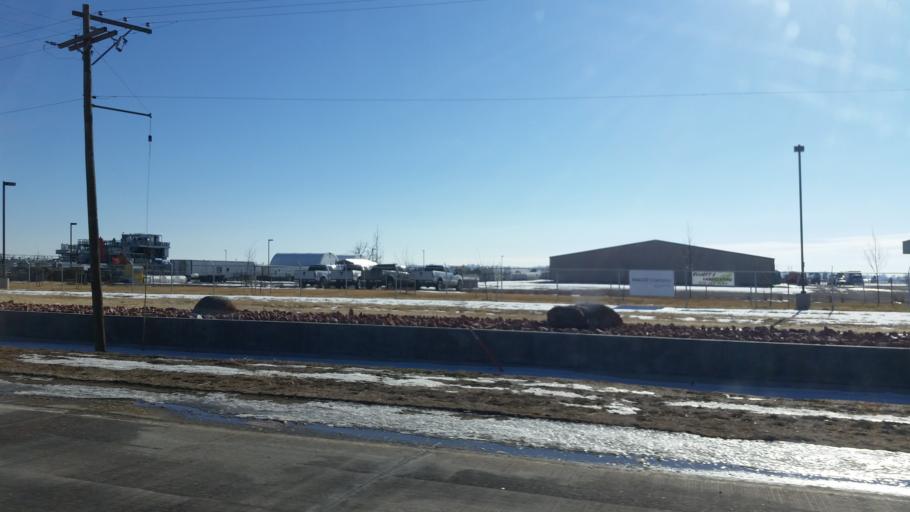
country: US
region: Colorado
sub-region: Weld County
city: Kersey
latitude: 40.3920
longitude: -104.6167
